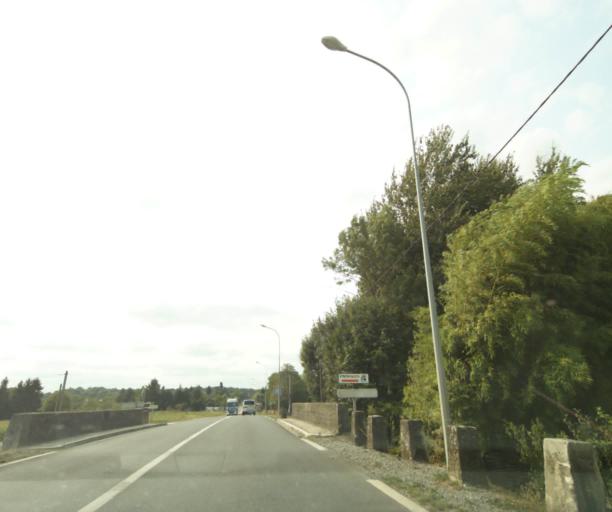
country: FR
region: Centre
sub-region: Departement de l'Indre
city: Clion
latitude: 46.9422
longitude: 1.2259
